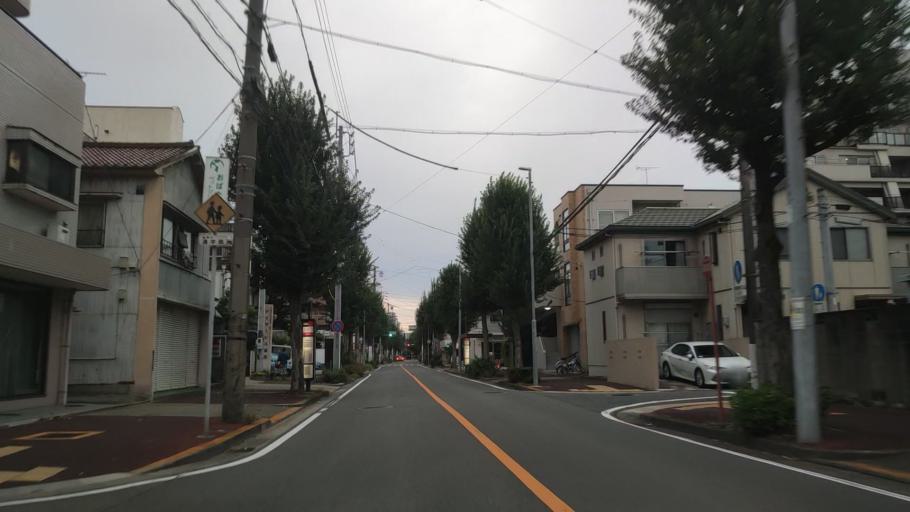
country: JP
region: Aichi
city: Nagoya-shi
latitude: 35.1885
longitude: 136.8957
